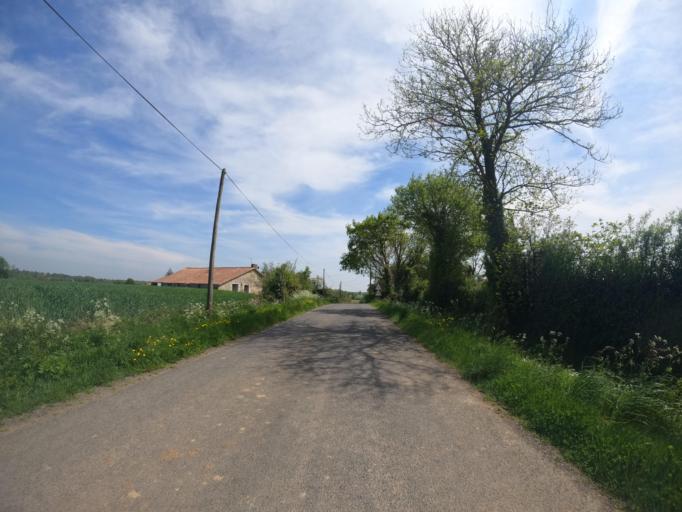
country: FR
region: Poitou-Charentes
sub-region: Departement des Deux-Sevres
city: Moncoutant
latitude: 46.6686
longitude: -0.5210
